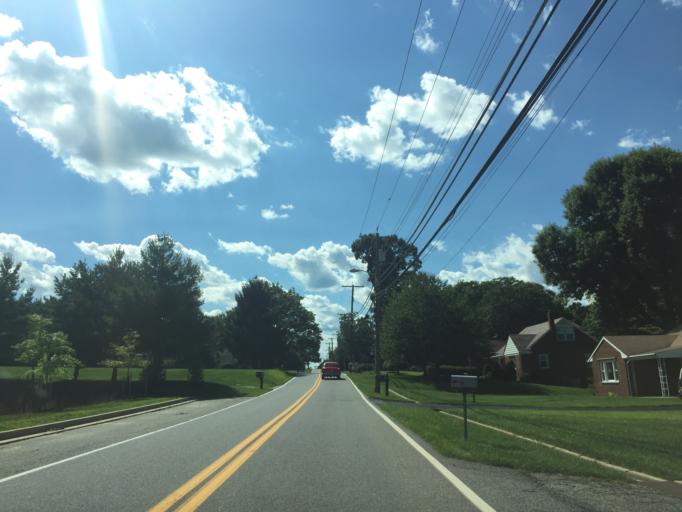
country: US
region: Maryland
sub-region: Baltimore County
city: Perry Hall
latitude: 39.4159
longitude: -76.4458
